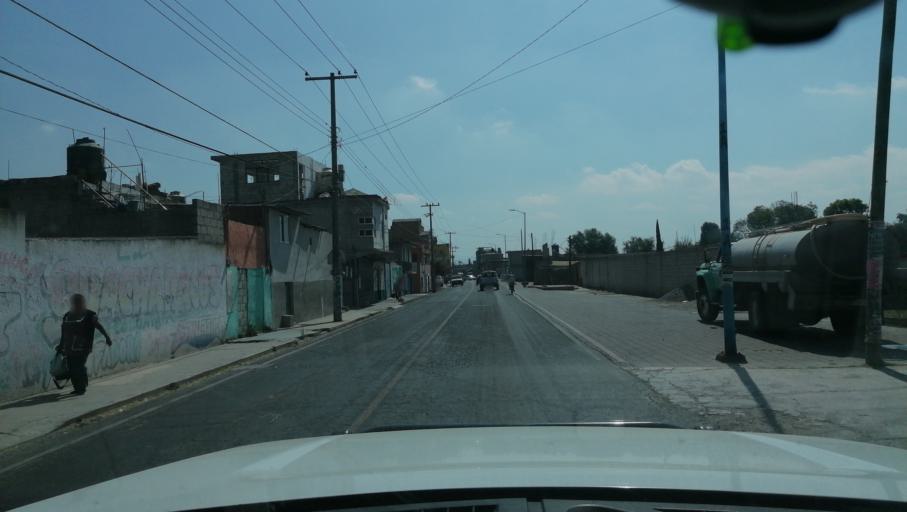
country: MX
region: Tlaxcala
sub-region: Tetlatlahuca
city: Tetlatlahuca
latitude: 19.2321
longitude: -98.2979
